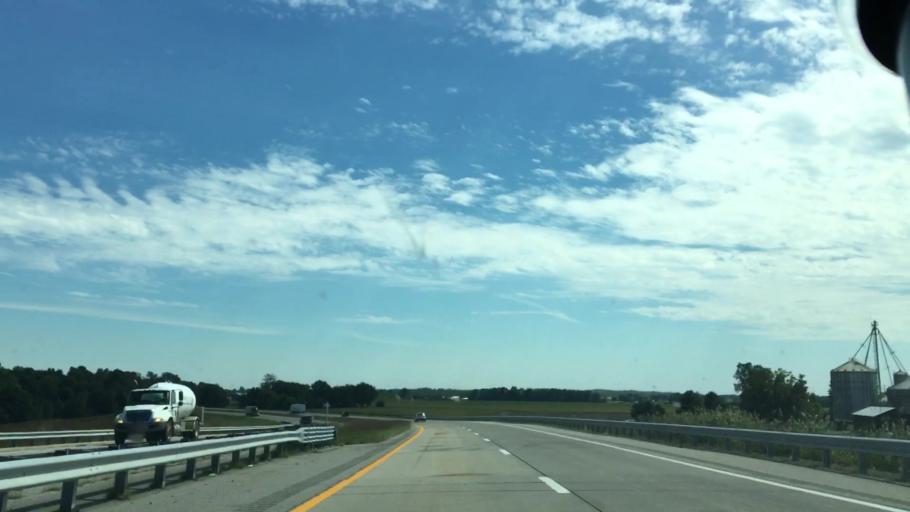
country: US
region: Kentucky
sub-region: Daviess County
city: Owensboro
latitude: 37.7545
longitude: -87.2949
